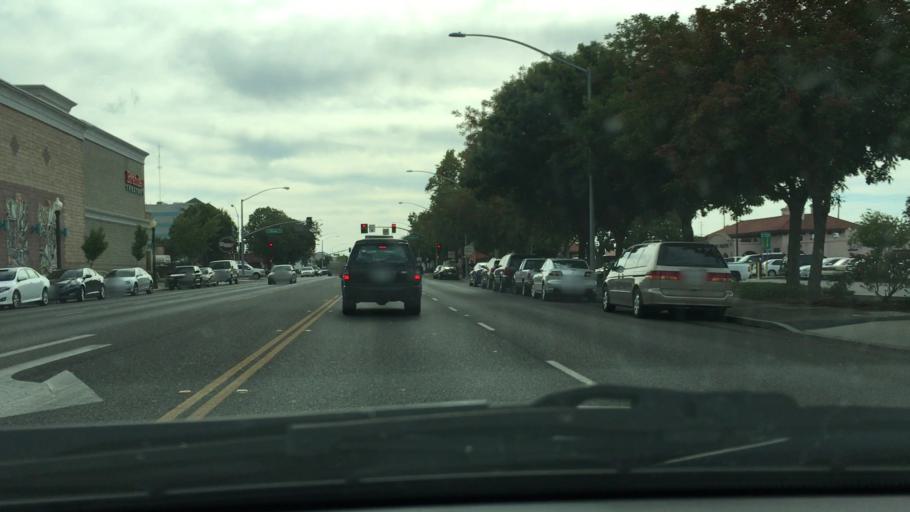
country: US
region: California
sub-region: Stanislaus County
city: Modesto
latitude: 37.6405
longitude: -121.0023
